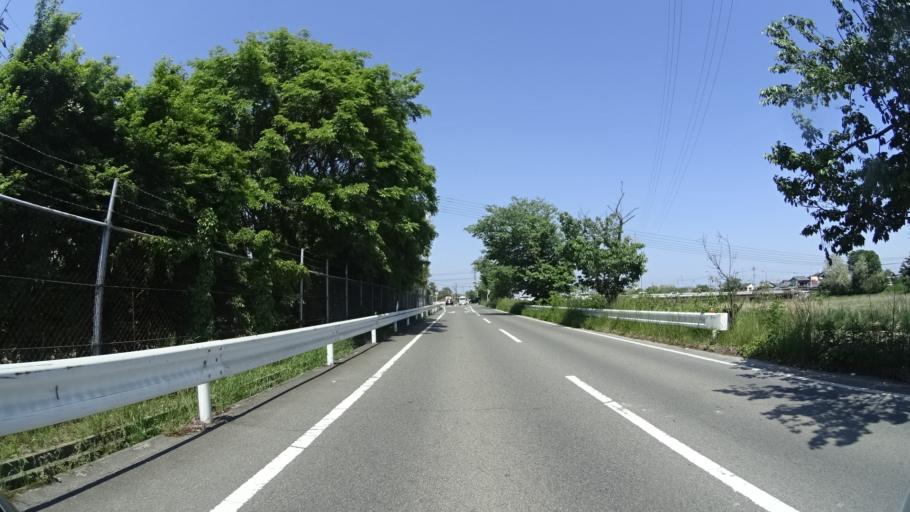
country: JP
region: Ehime
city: Hojo
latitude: 34.0491
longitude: 132.9879
